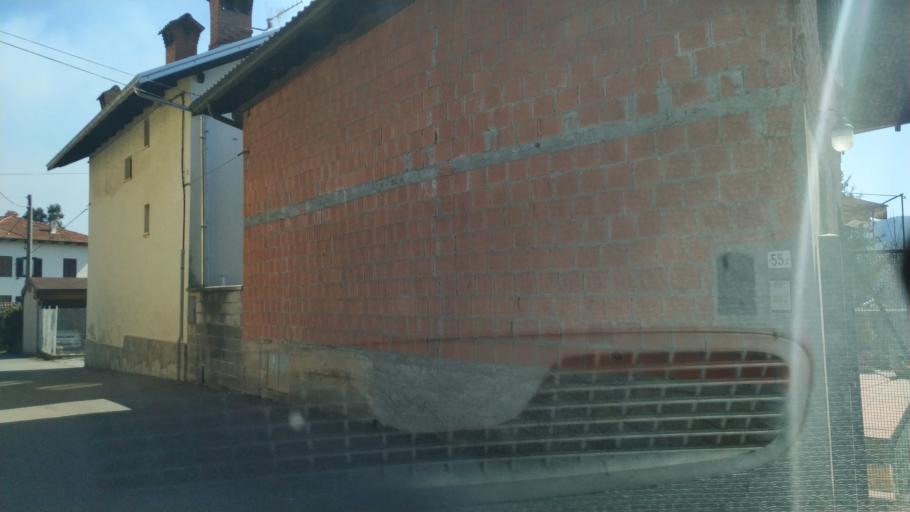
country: IT
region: Piedmont
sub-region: Provincia di Biella
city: Pray
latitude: 45.6781
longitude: 8.2088
